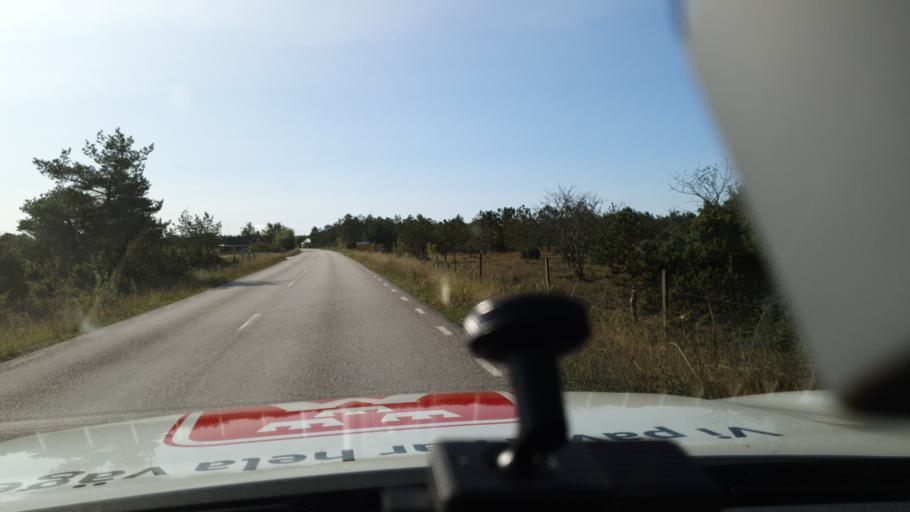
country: SE
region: Gotland
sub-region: Gotland
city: Hemse
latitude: 57.1212
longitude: 18.2756
